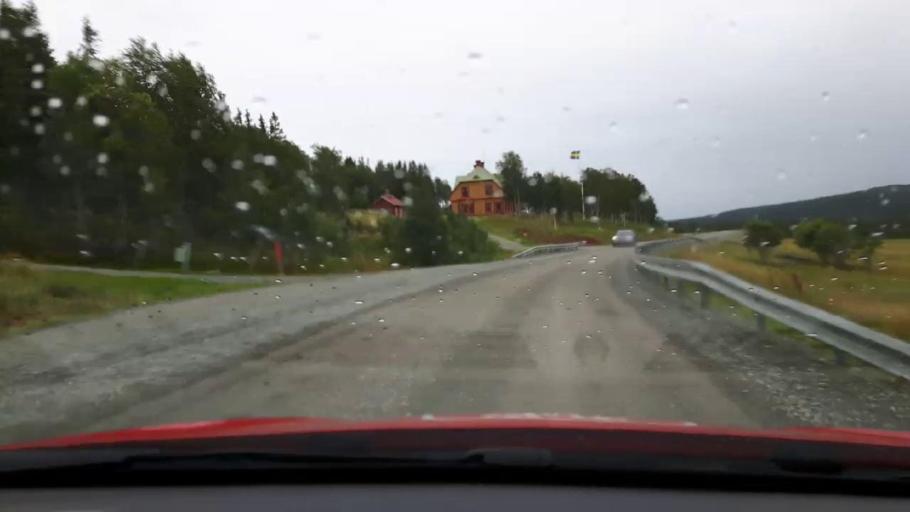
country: NO
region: Nord-Trondelag
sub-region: Meraker
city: Meraker
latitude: 63.5221
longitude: 12.4043
